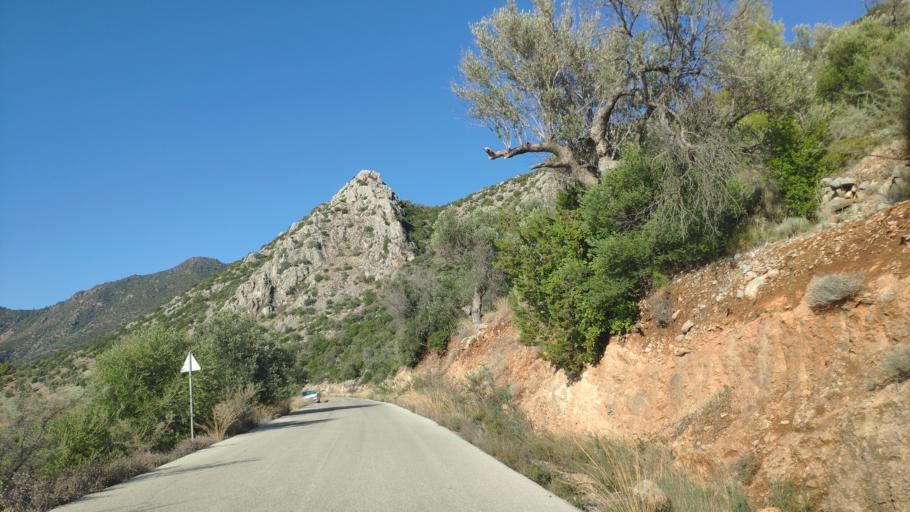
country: GR
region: Attica
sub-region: Nomos Piraios
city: Galatas
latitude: 37.5741
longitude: 23.3598
